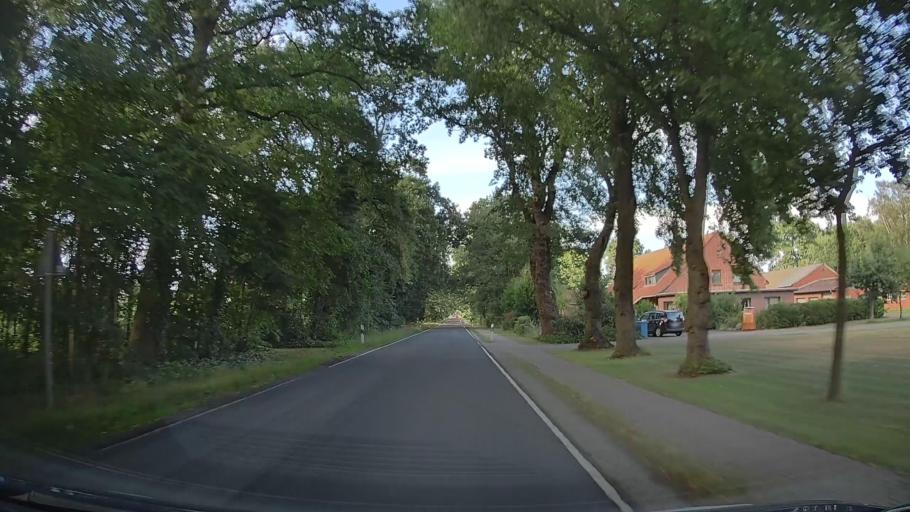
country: DE
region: Lower Saxony
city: Molbergen
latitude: 52.9269
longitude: 7.8921
